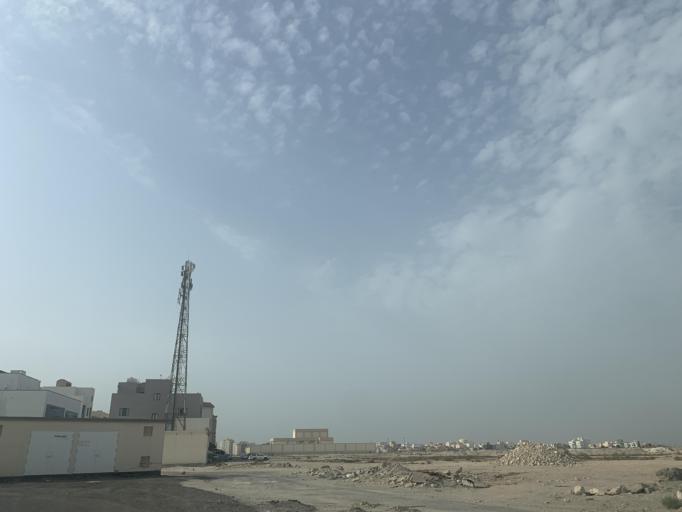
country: BH
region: Northern
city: Madinat `Isa
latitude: 26.1795
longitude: 50.4822
